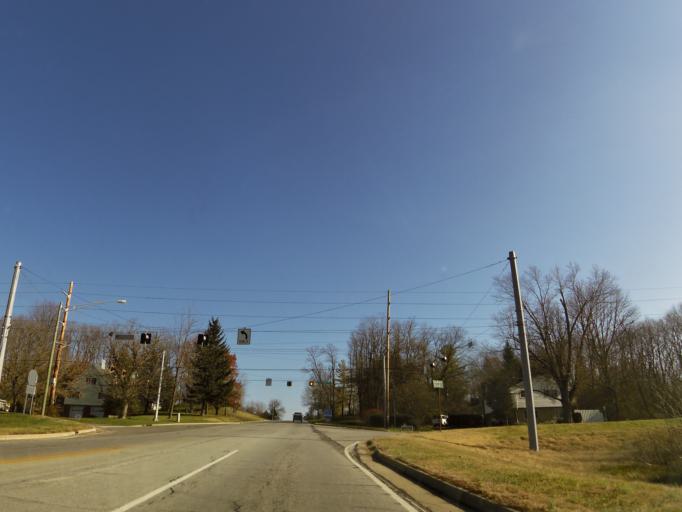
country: US
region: Indiana
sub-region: Fayette County
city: Connersville
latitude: 39.6383
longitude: -85.1677
